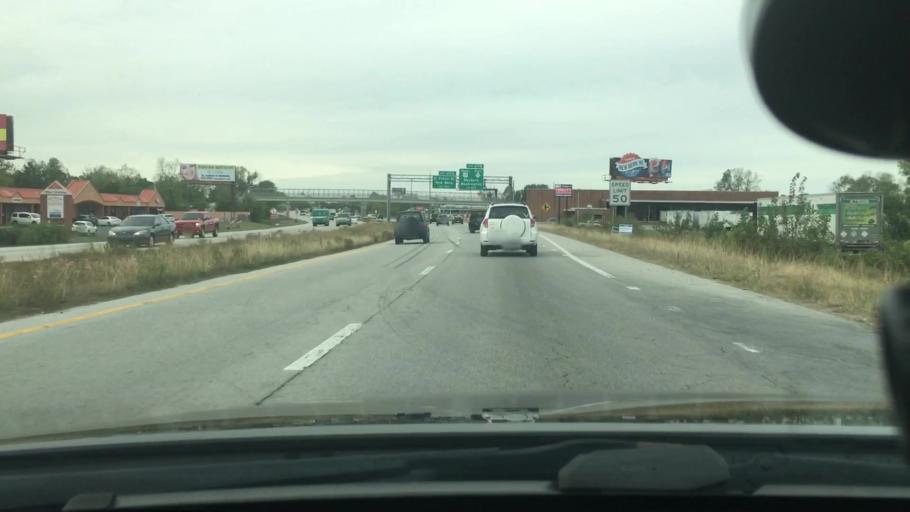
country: US
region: North Carolina
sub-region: Craven County
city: James City
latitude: 35.0851
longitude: -77.0322
